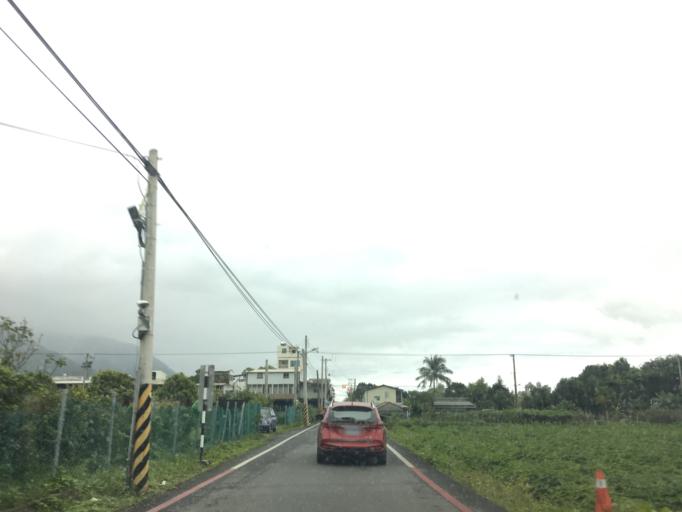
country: TW
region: Taiwan
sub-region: Hualien
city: Hualian
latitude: 23.9888
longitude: 121.5700
